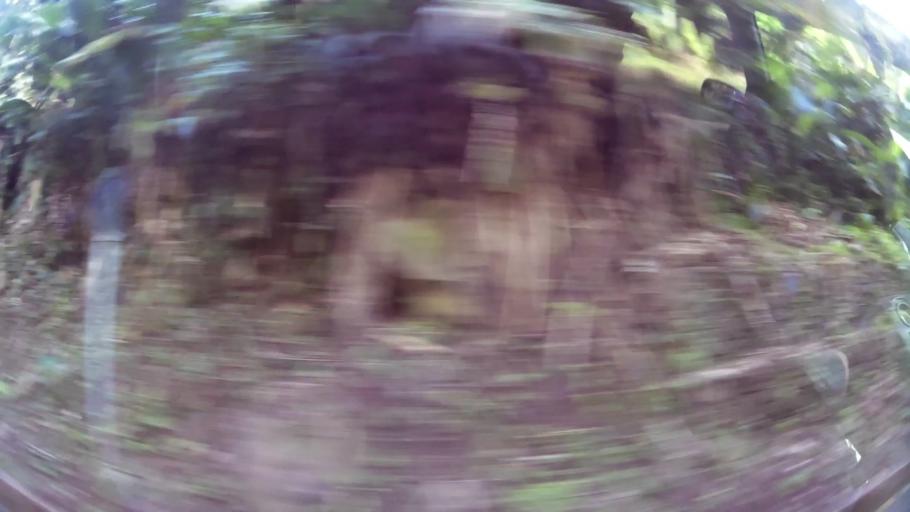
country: DM
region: Saint Paul
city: Mahaut
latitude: 15.3411
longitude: -61.3783
